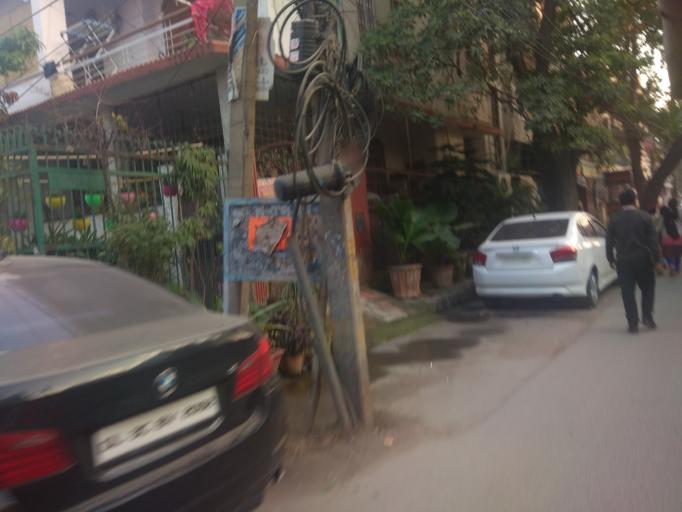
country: IN
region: NCT
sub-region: West Delhi
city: Nangloi Jat
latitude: 28.6311
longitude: 77.0764
